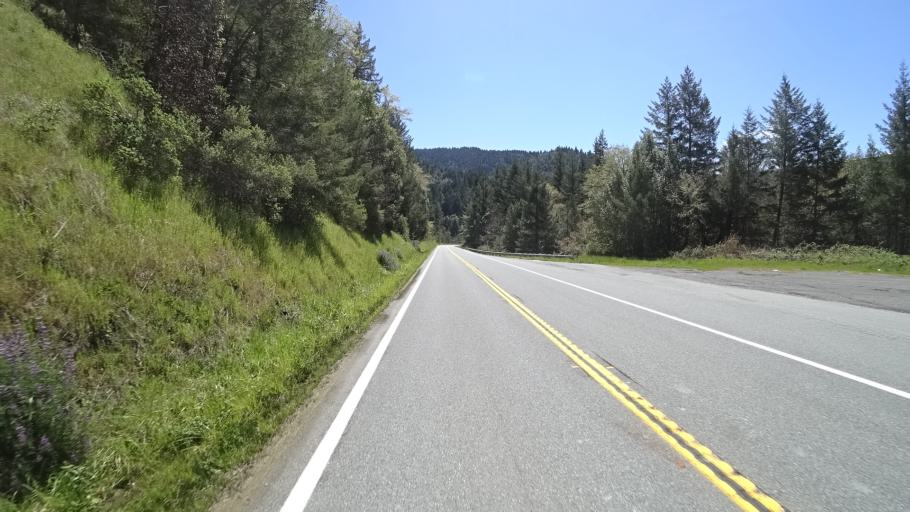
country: US
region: California
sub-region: Humboldt County
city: Willow Creek
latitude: 40.9062
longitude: -123.8064
